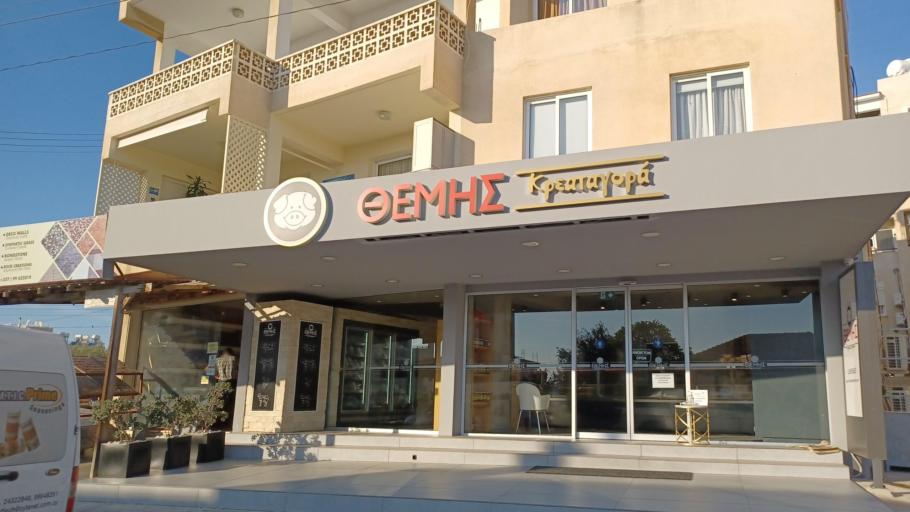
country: CY
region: Pafos
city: Paphos
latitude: 34.7753
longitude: 32.4348
